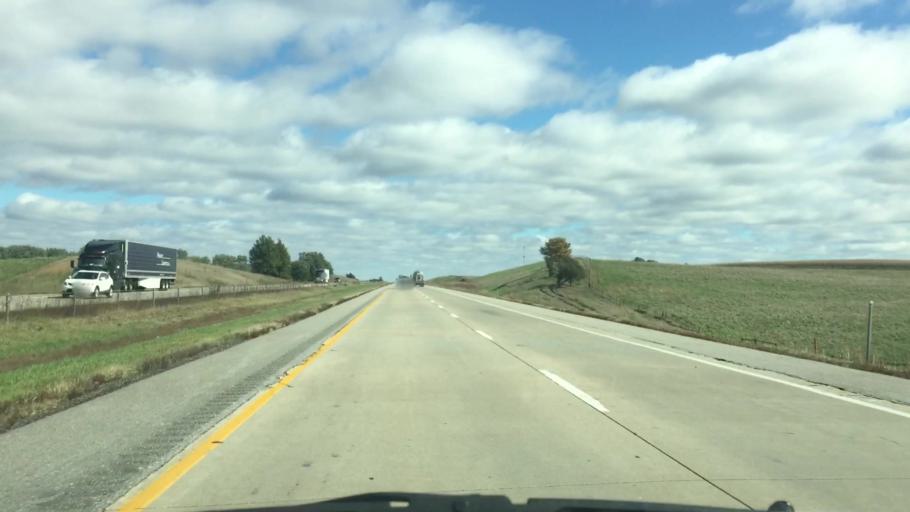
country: US
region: Iowa
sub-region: Poweshiek County
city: Brooklyn
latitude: 41.6943
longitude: -92.4832
